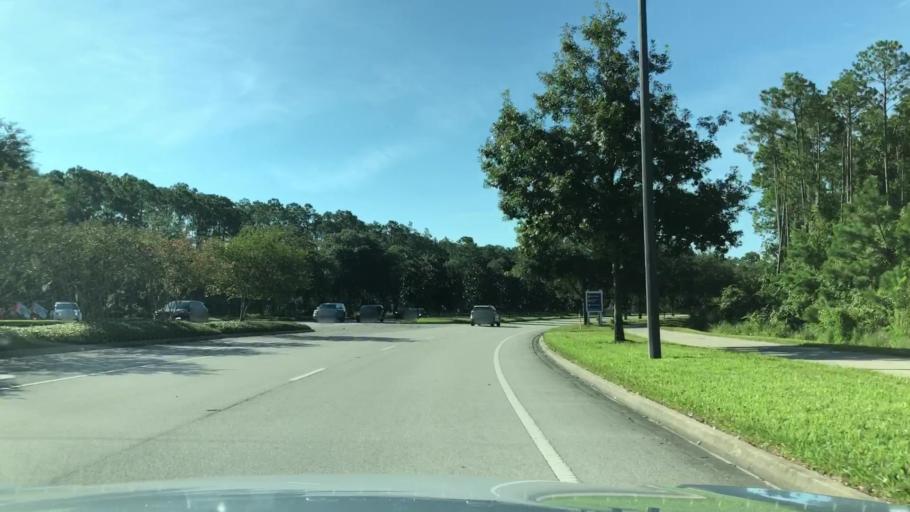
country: US
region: Florida
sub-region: Saint Johns County
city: Palm Valley
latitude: 30.1008
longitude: -81.4108
